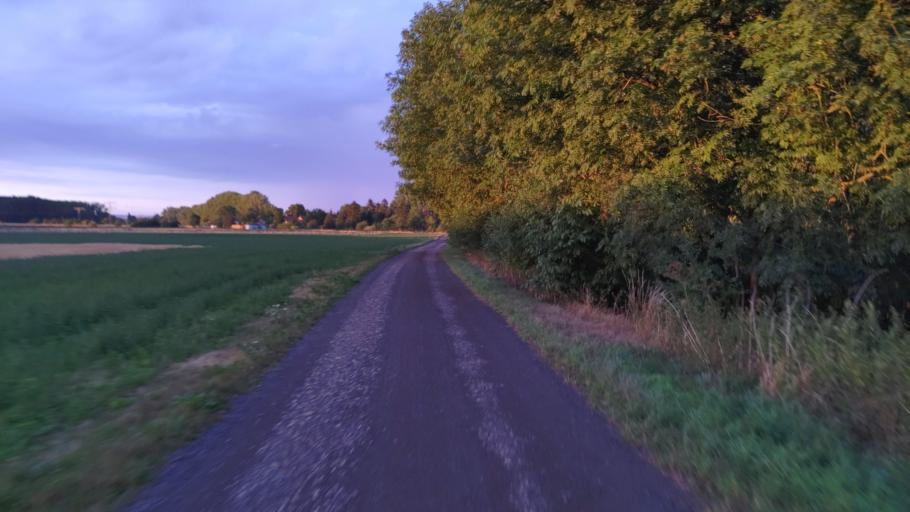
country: DE
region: Thuringia
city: Kleinmolsen
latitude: 50.9853
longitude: 11.0969
